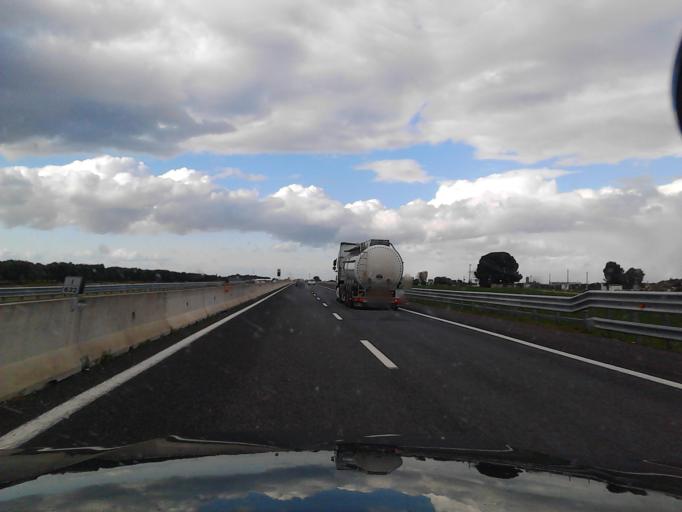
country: IT
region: Apulia
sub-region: Provincia di Barletta - Andria - Trani
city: Andria
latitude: 41.2446
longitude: 16.3514
